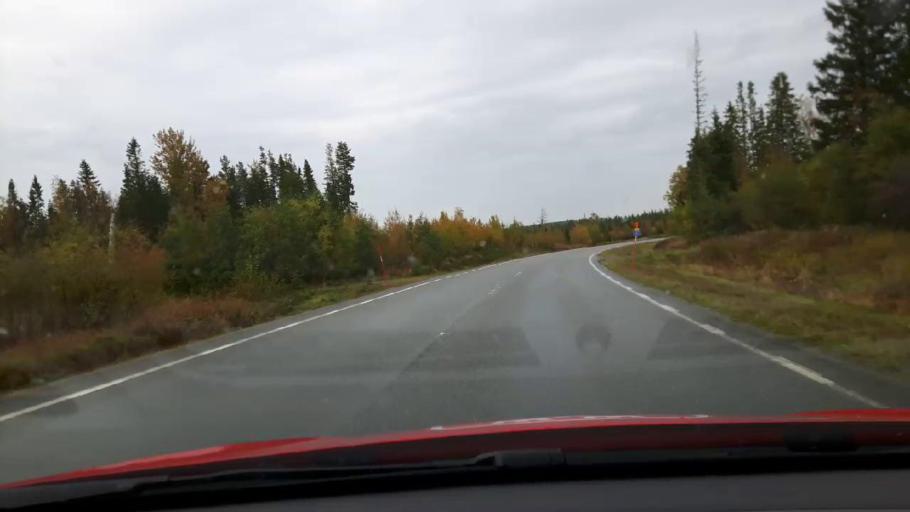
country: SE
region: Jaemtland
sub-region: Bergs Kommun
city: Hoverberg
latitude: 62.9172
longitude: 14.3283
